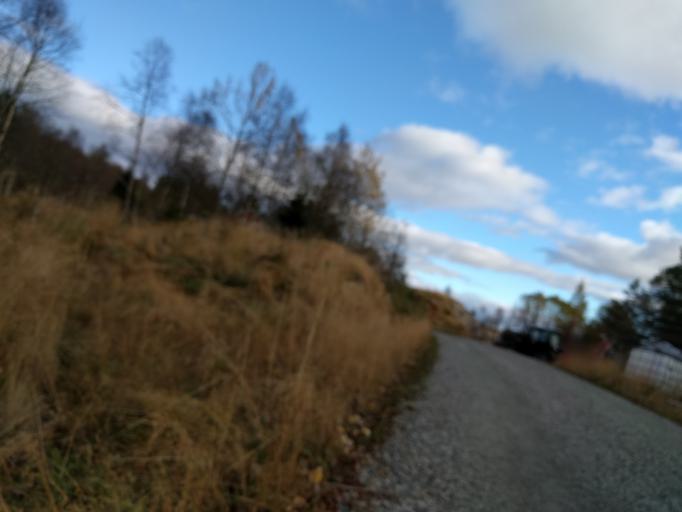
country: NO
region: Aust-Agder
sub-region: Evje og Hornnes
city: Evje
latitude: 58.6526
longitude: 7.9482
